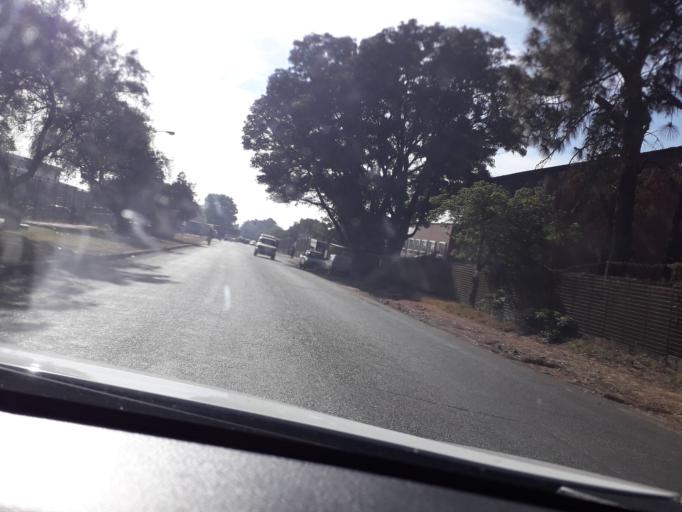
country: ZA
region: Gauteng
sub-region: Ekurhuleni Metropolitan Municipality
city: Germiston
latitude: -26.1670
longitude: 28.1915
